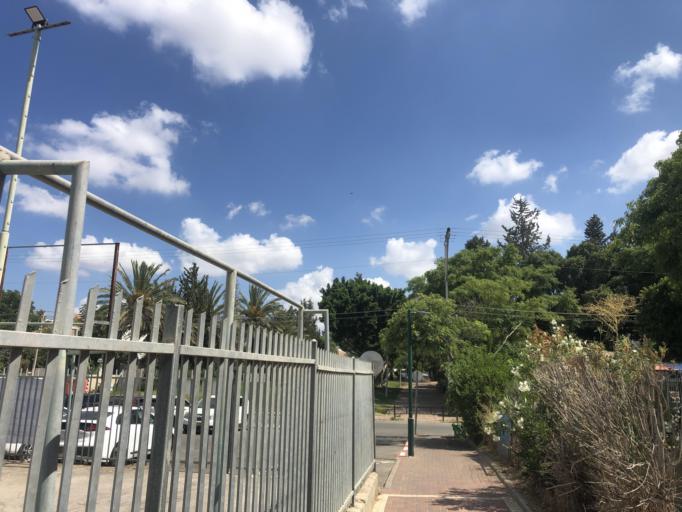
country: IL
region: Central District
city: Yehud
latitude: 32.0302
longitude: 34.8950
